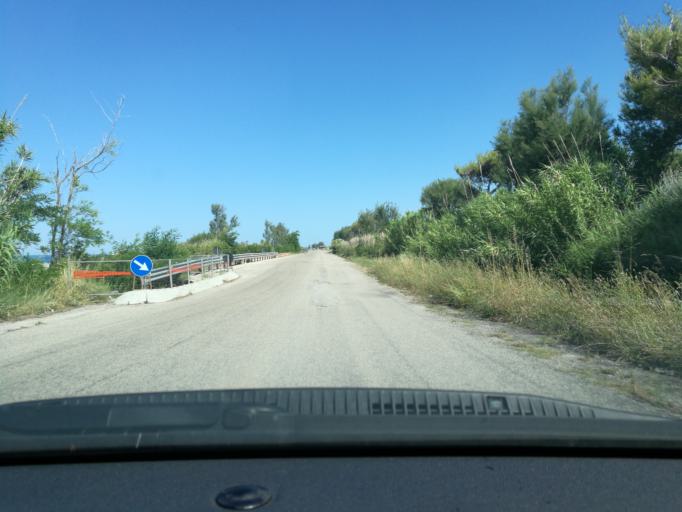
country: IT
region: Abruzzo
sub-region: Provincia di Chieti
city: Vasto
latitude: 42.1747
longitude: 14.6955
